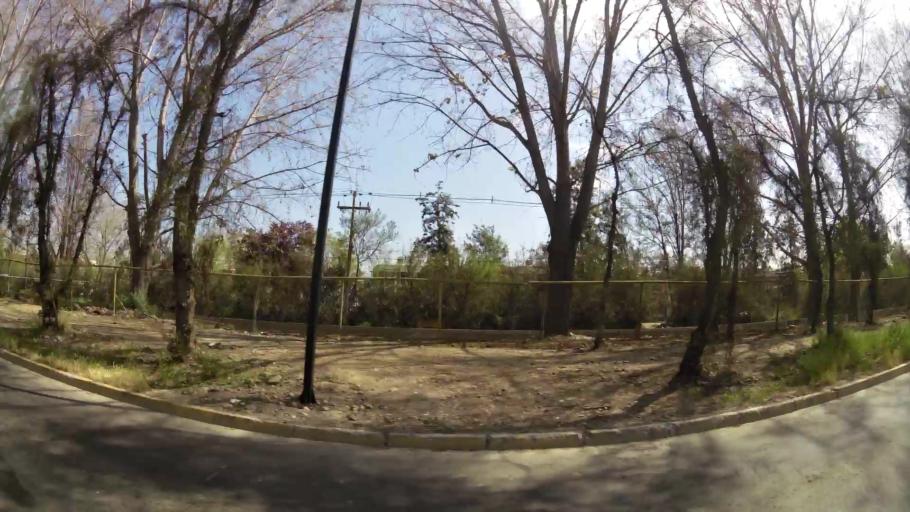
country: CL
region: Santiago Metropolitan
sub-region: Provincia de Santiago
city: Villa Presidente Frei, Nunoa, Santiago, Chile
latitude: -33.4683
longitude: -70.5507
